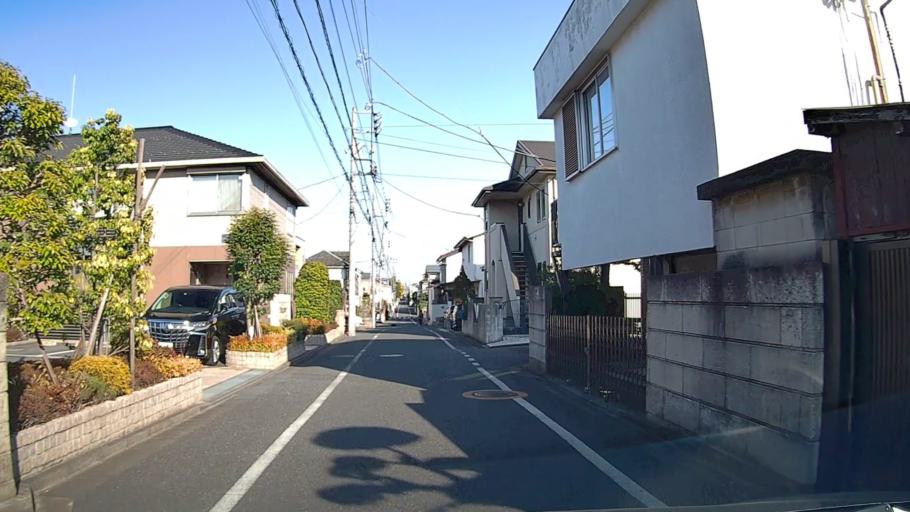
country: JP
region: Saitama
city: Asaka
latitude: 35.7697
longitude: 139.5910
